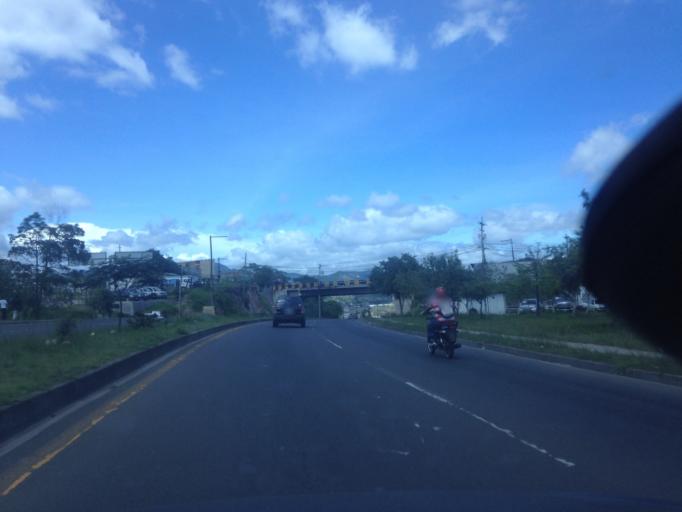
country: HN
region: Francisco Morazan
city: Yaguacire
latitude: 14.0450
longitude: -87.2232
